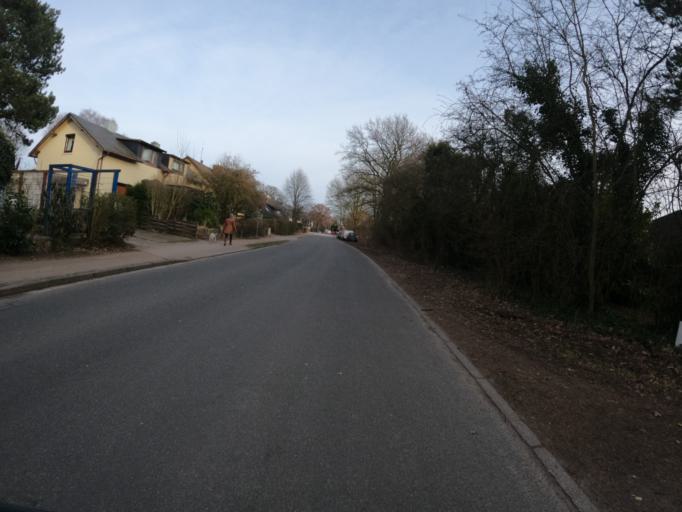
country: DE
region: Schleswig-Holstein
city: Halstenbek
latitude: 53.5769
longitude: 9.8404
